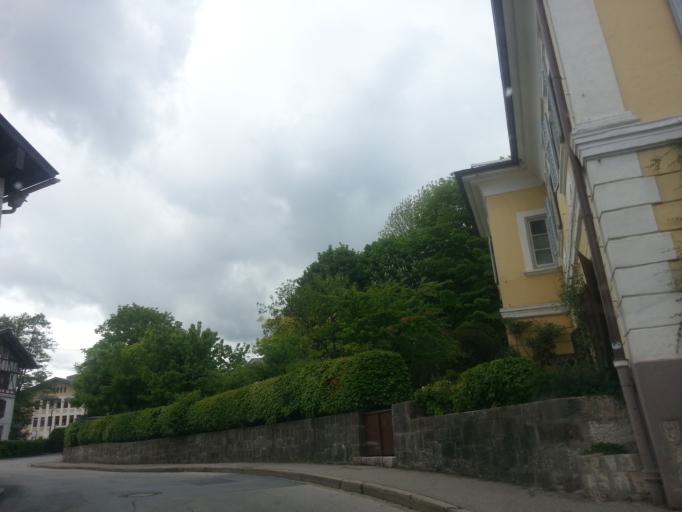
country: DE
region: Bavaria
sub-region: Upper Bavaria
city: Berchtesgaden
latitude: 47.6341
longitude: 13.0068
